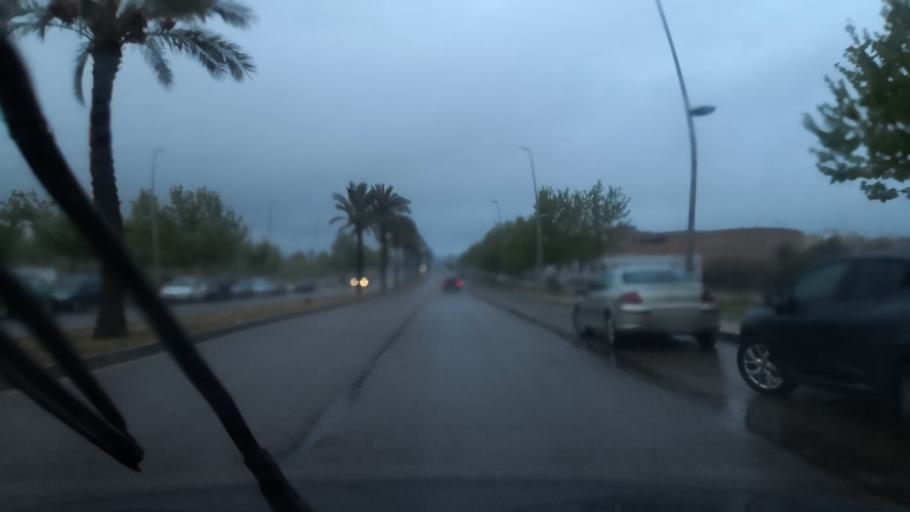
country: ES
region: Extremadura
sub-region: Provincia de Badajoz
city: Merida
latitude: 38.9131
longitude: -6.3647
